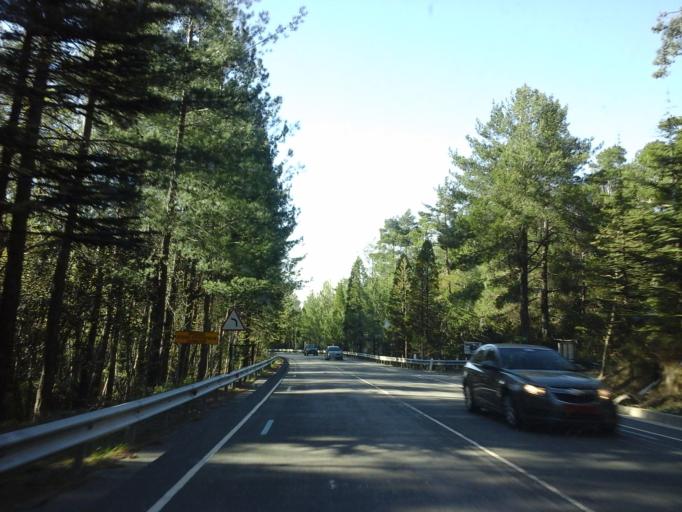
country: CY
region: Limassol
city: Kyperounta
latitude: 34.9475
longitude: 32.9295
